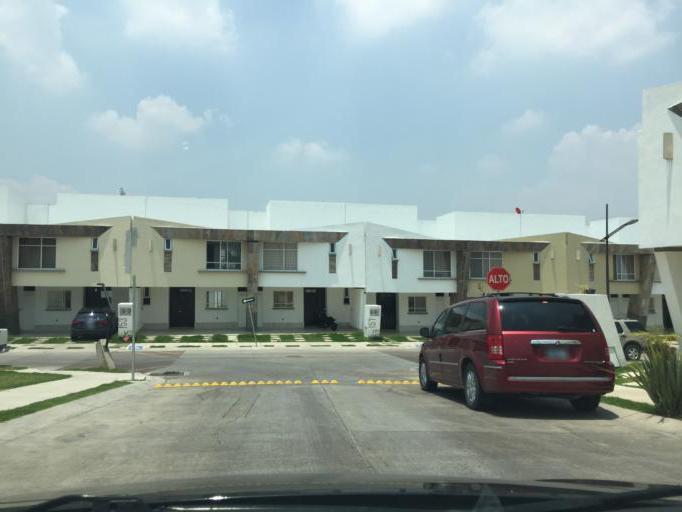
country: MX
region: Guanajuato
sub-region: Leon
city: La Ermita
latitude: 21.1679
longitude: -101.7343
